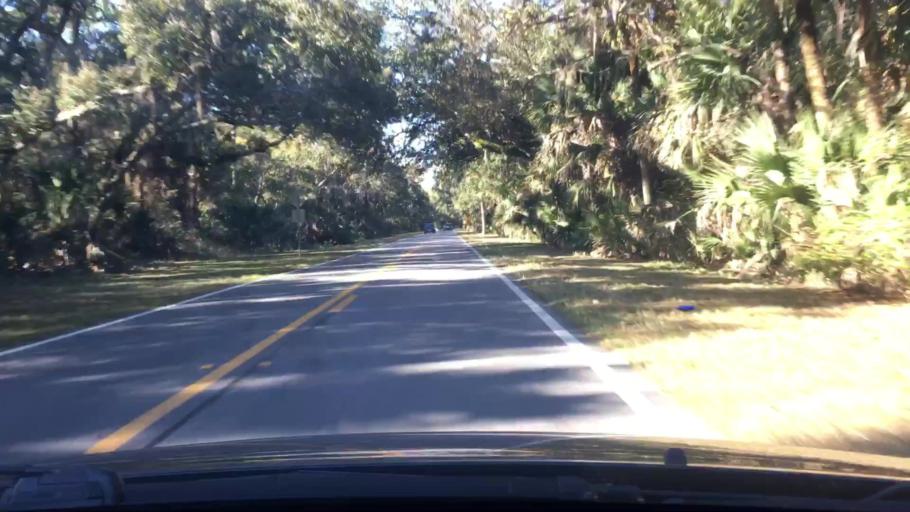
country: US
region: Florida
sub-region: Volusia County
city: Ormond-by-the-Sea
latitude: 29.3616
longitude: -81.1220
